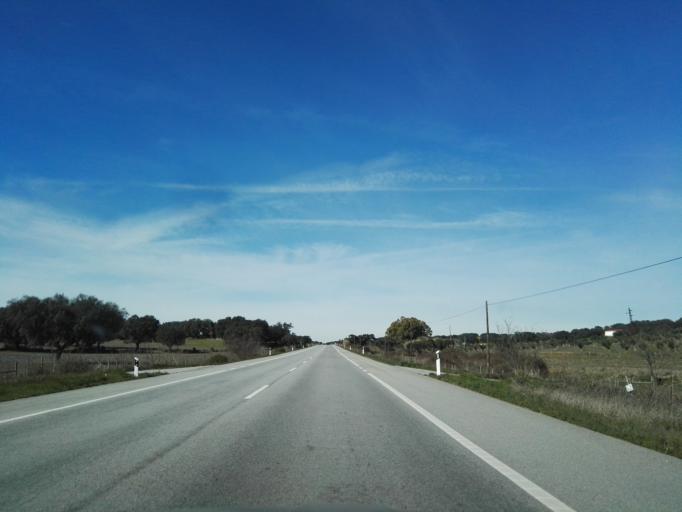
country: PT
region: Portalegre
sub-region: Arronches
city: Arronches
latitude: 39.1634
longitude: -7.3245
